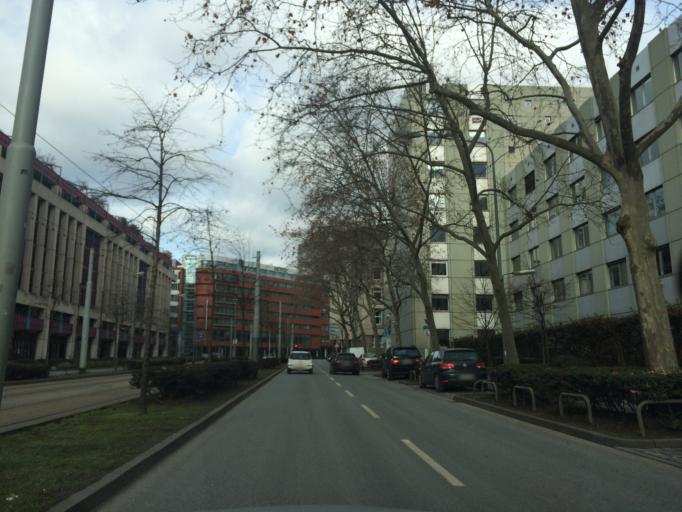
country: DE
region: Hesse
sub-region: Regierungsbezirk Darmstadt
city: Frankfurt am Main
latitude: 50.1157
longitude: 8.6878
